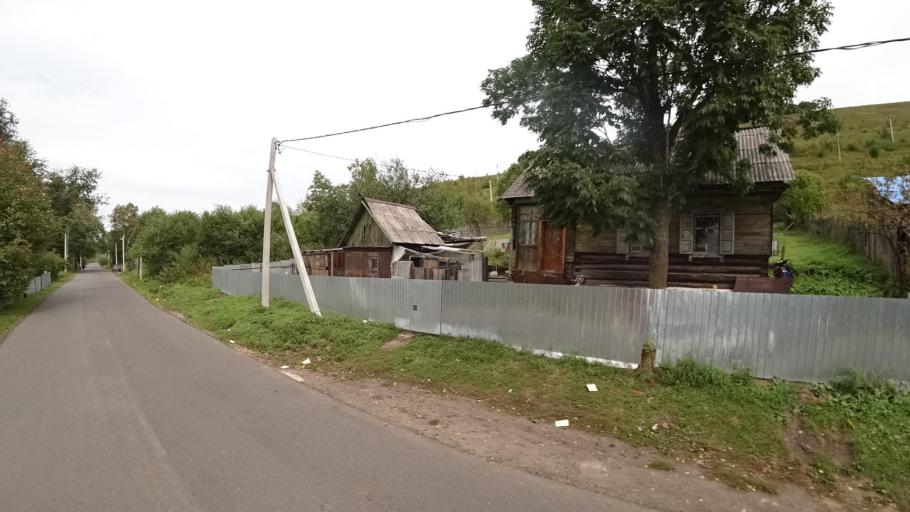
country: RU
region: Jewish Autonomous Oblast
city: Khingansk
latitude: 49.0269
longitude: 131.0588
